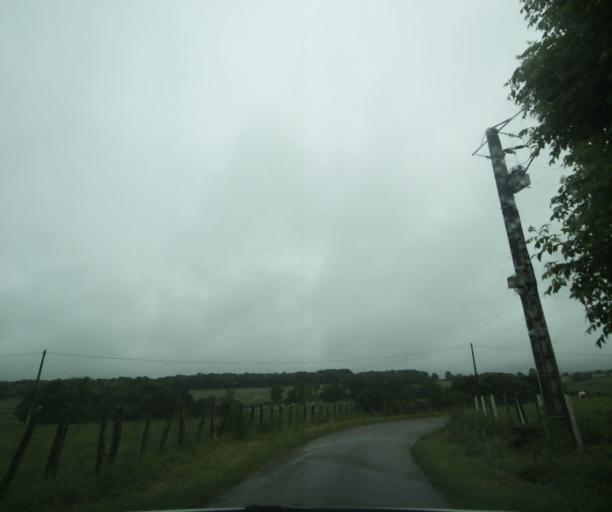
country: FR
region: Bourgogne
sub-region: Departement de Saone-et-Loire
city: Charolles
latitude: 46.4724
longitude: 4.2196
